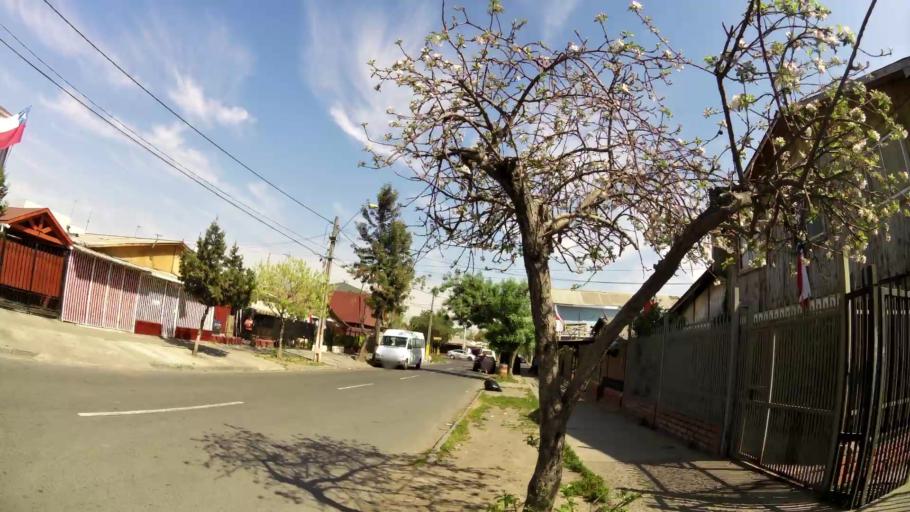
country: CL
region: Santiago Metropolitan
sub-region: Provincia de Santiago
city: La Pintana
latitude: -33.5613
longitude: -70.6558
